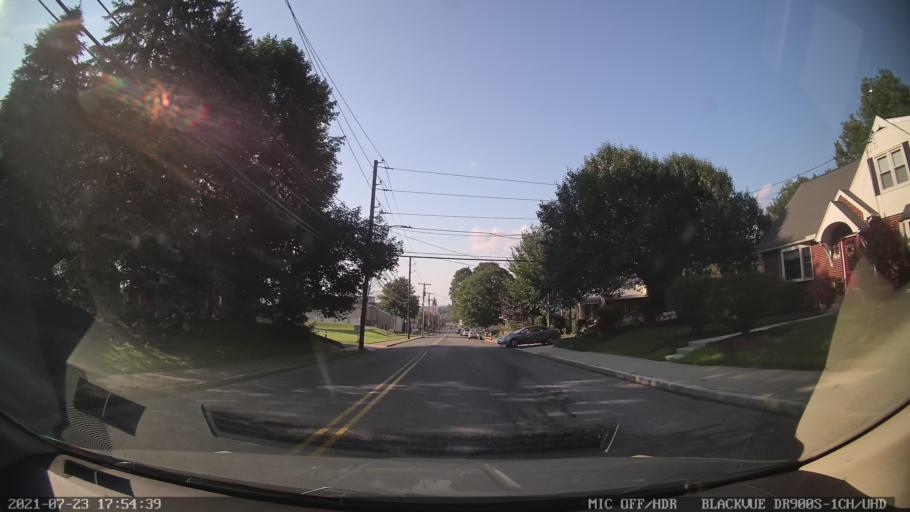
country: US
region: Pennsylvania
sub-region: Lehigh County
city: Macungie
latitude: 40.5107
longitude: -75.5551
